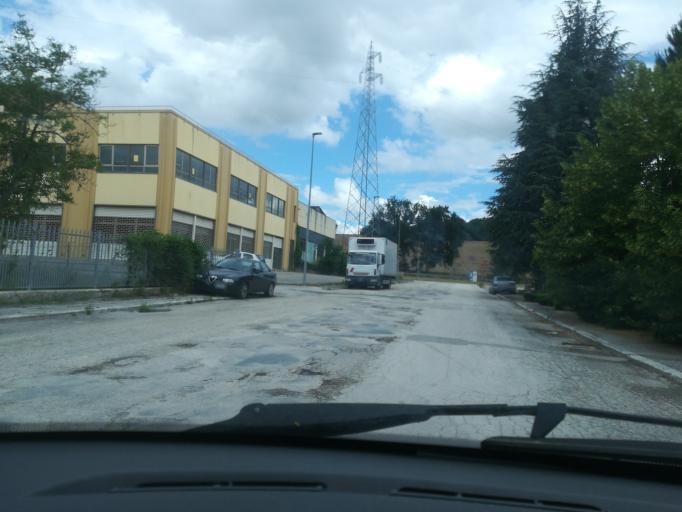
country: IT
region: The Marches
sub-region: Provincia di Macerata
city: Sforzacosta
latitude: 43.2586
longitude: 13.4271
